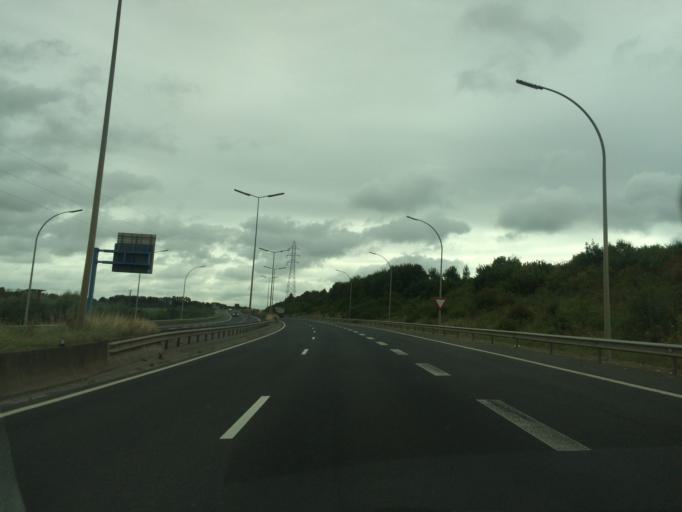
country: LU
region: Luxembourg
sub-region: Canton d'Esch-sur-Alzette
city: Schifflange
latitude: 49.5126
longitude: 6.0176
